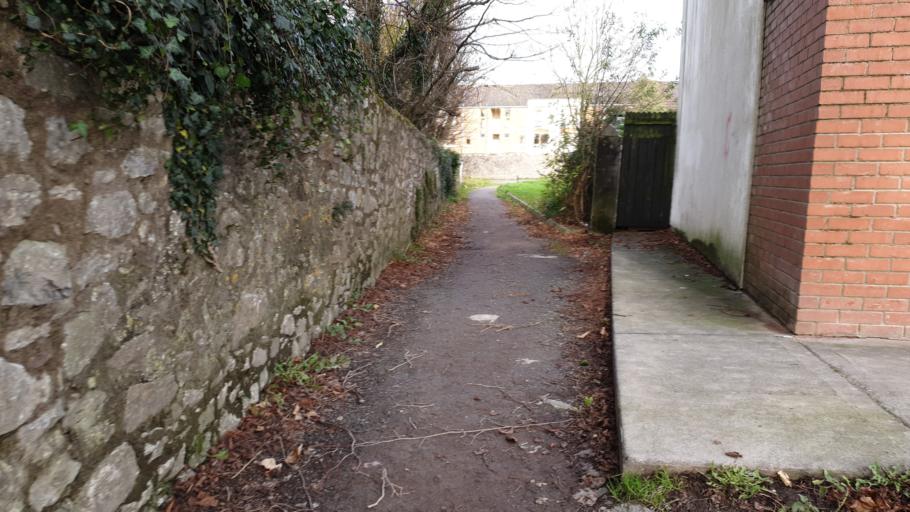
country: IE
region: Munster
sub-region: County Cork
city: Cork
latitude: 51.8935
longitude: -8.4110
